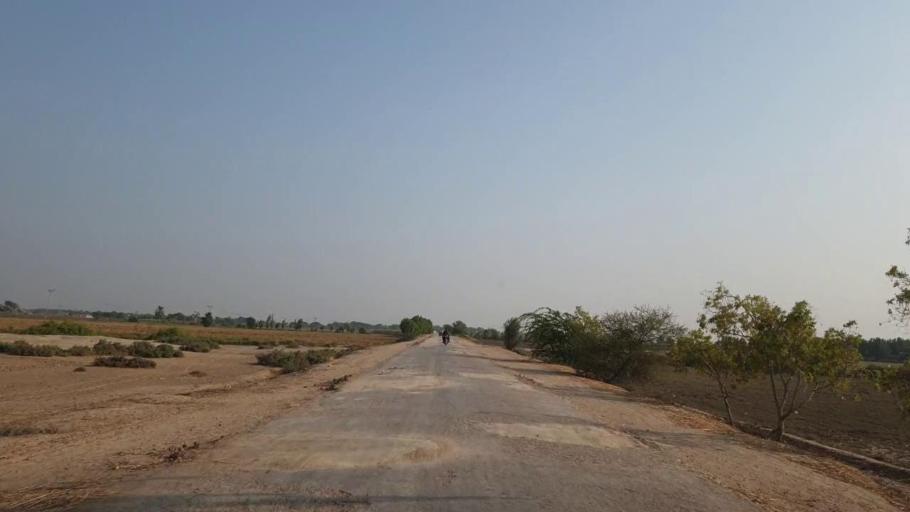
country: PK
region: Sindh
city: Bulri
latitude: 24.9939
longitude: 68.3840
